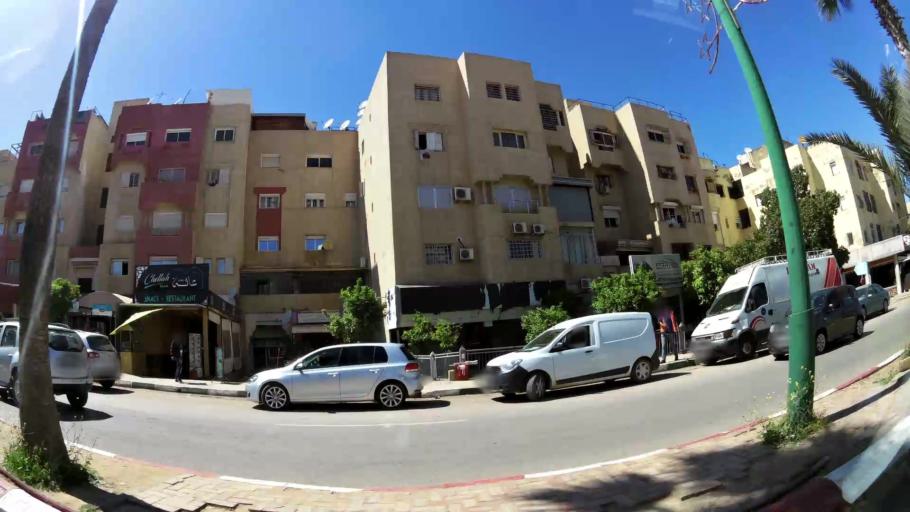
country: MA
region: Meknes-Tafilalet
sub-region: Meknes
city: Meknes
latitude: 33.8907
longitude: -5.5770
